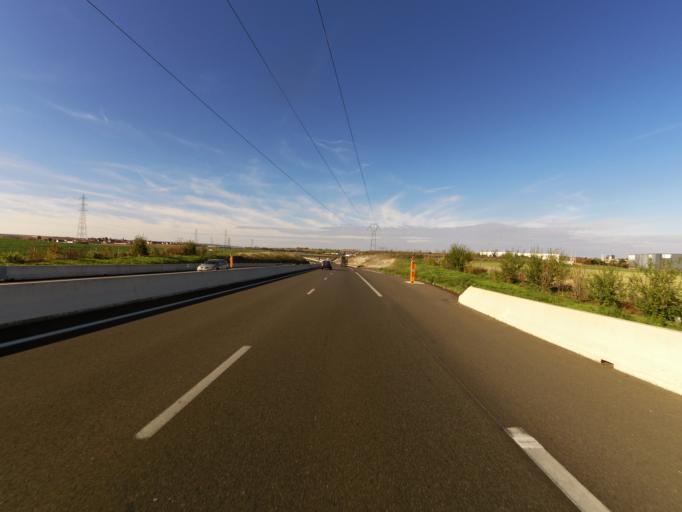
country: FR
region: Champagne-Ardenne
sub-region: Departement de la Marne
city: Cormontreuil
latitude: 49.2102
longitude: 4.0563
